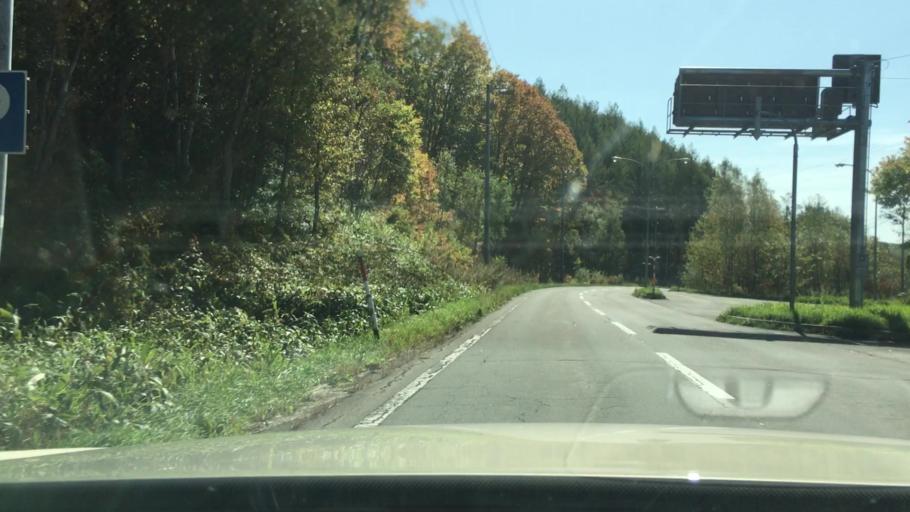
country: JP
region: Hokkaido
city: Kitami
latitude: 43.5871
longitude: 143.6827
